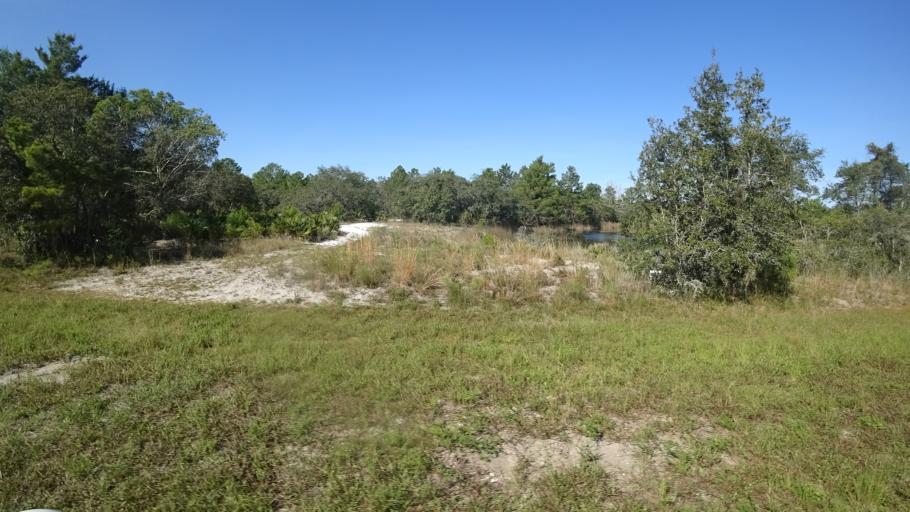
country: US
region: Florida
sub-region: Sarasota County
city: Lake Sarasota
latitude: 27.3586
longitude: -82.2375
